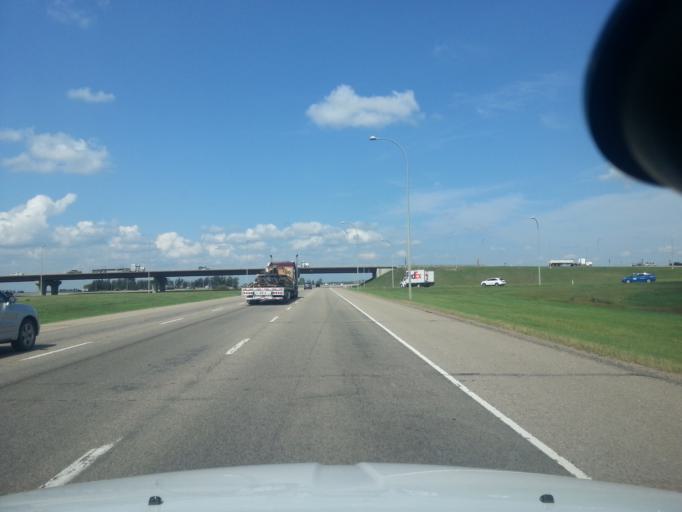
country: CA
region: Alberta
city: Leduc
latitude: 53.3355
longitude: -113.5478
